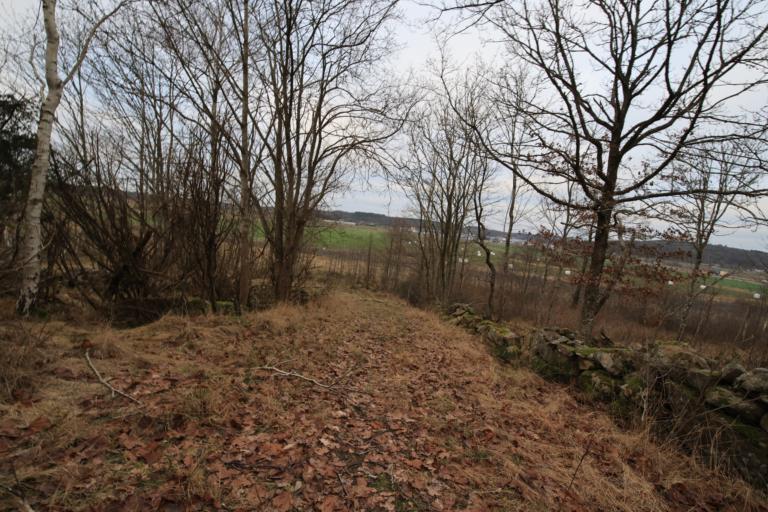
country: SE
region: Halland
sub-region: Varbergs Kommun
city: Varberg
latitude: 57.1536
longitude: 12.2871
